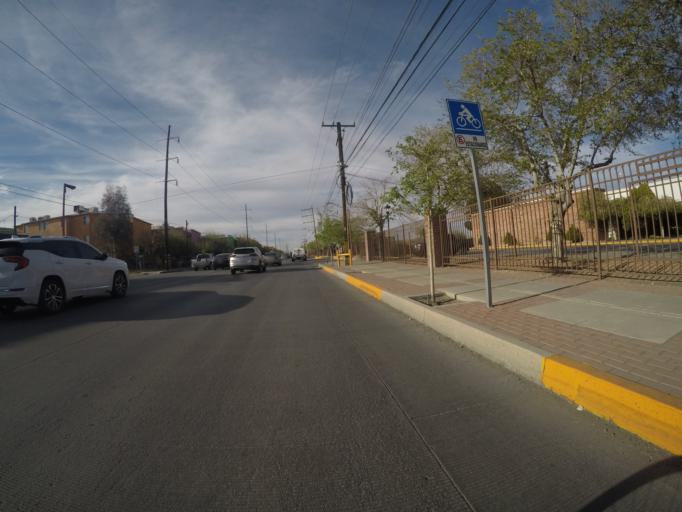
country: MX
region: Chihuahua
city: Ciudad Juarez
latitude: 31.7494
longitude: -106.4411
